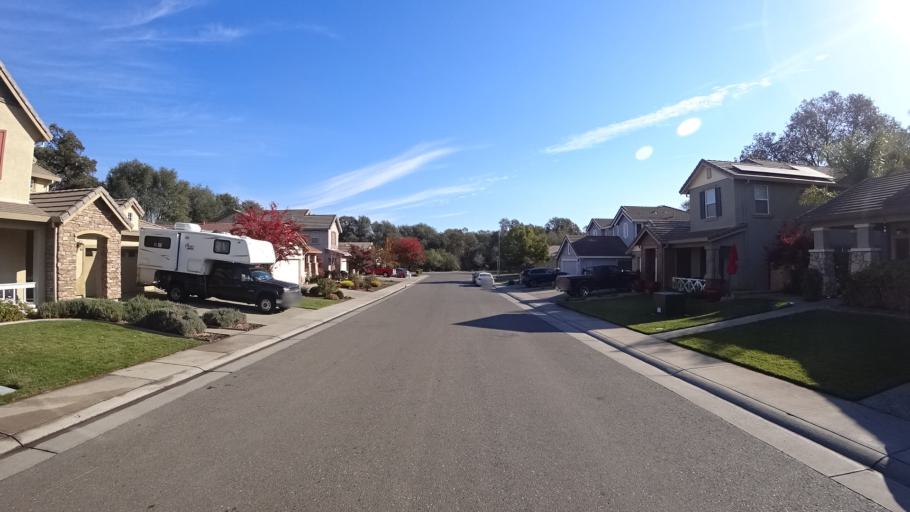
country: US
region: California
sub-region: Sacramento County
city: Citrus Heights
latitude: 38.6865
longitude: -121.2938
